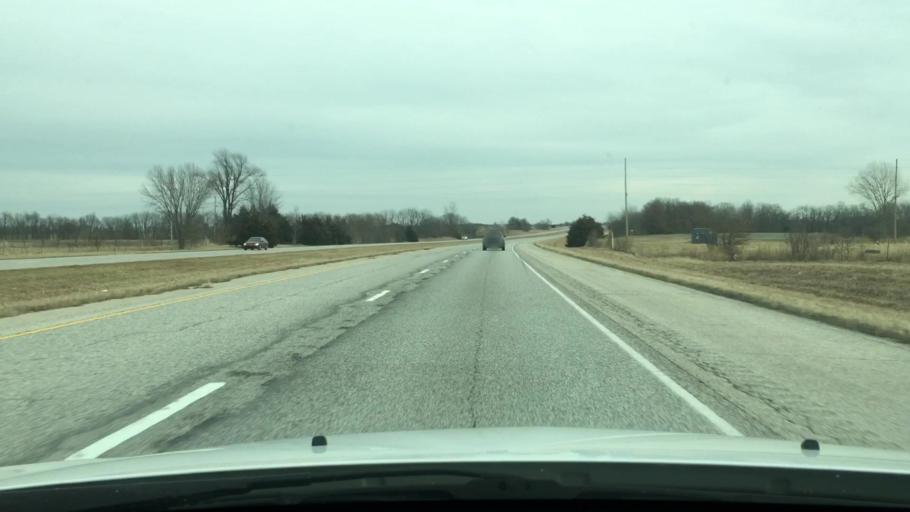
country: US
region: Illinois
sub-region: Pike County
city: Griggsville
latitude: 39.6778
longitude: -90.7256
